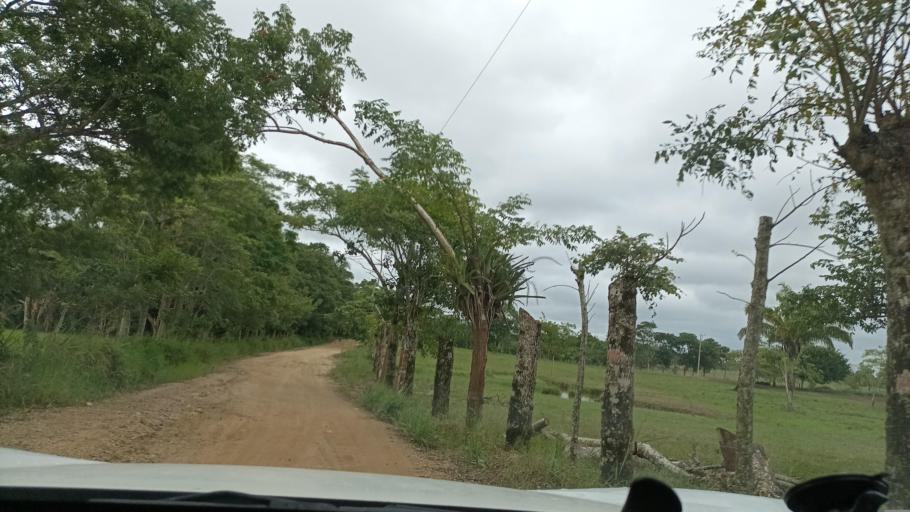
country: MX
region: Veracruz
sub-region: Moloacan
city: Cuichapa
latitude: 17.7958
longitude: -94.3758
